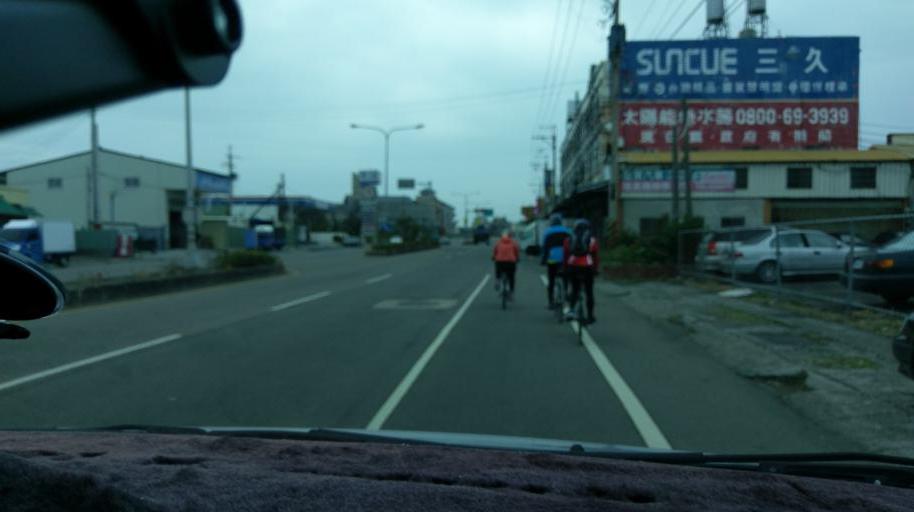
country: TW
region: Taiwan
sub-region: Miaoli
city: Miaoli
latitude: 24.4530
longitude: 120.6580
